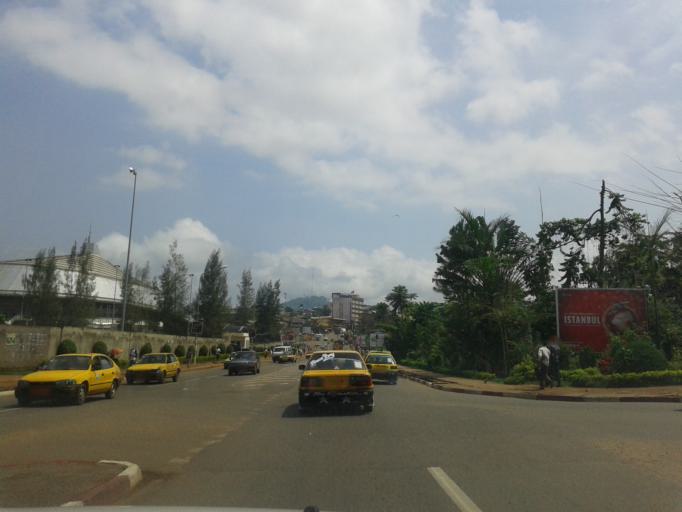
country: CM
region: Centre
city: Yaounde
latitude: 3.8732
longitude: 11.5140
